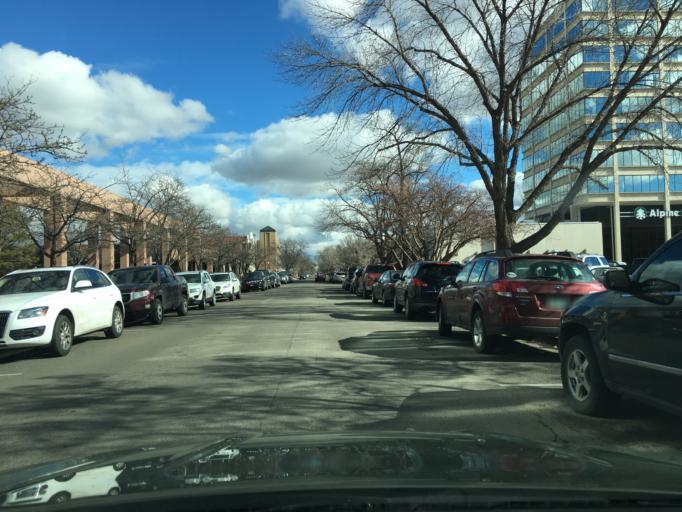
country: US
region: Colorado
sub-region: Mesa County
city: Grand Junction
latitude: 39.0693
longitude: -108.5659
